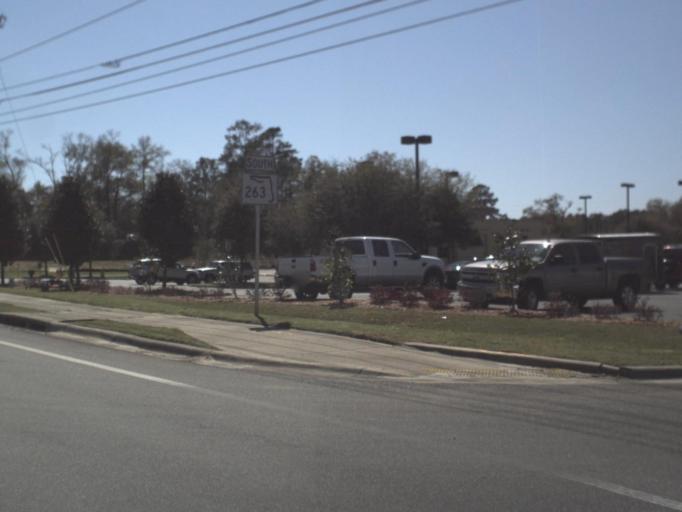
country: US
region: Florida
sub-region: Leon County
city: Tallahassee
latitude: 30.4576
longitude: -84.3611
